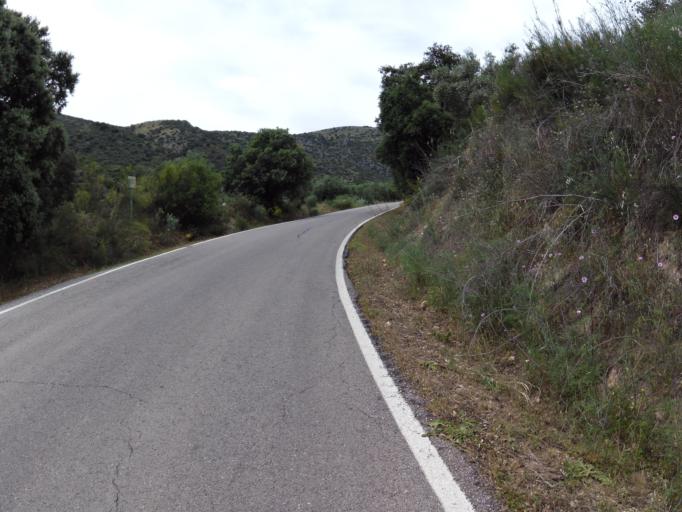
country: ES
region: Andalusia
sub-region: Province of Cordoba
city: Fuente-Tojar
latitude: 37.5185
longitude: -4.2125
